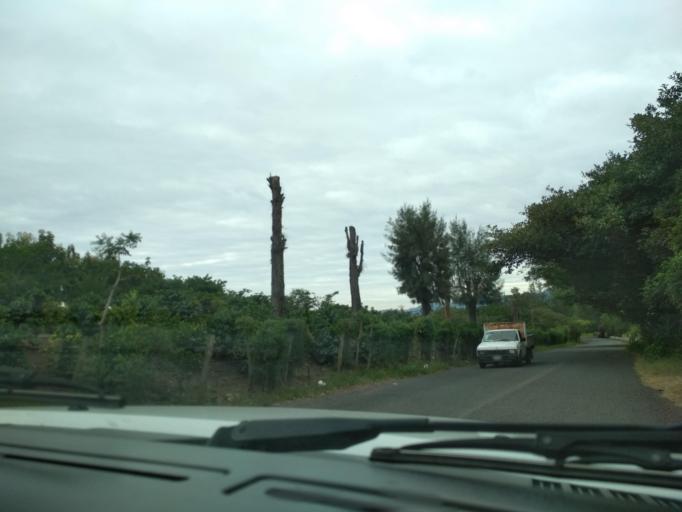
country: MX
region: Veracruz
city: Alto Lucero
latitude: 19.5966
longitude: -96.7947
